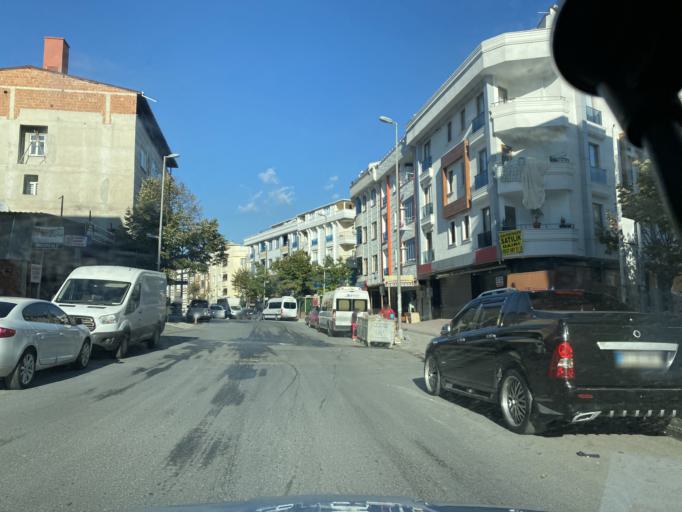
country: TR
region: Istanbul
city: Esenyurt
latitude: 41.0409
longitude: 28.6495
